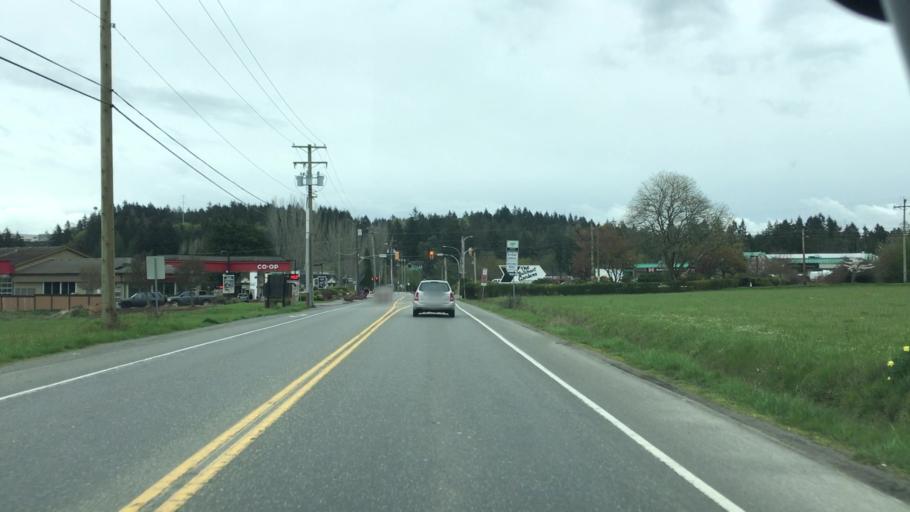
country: CA
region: British Columbia
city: North Saanich
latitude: 48.5664
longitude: -123.4396
